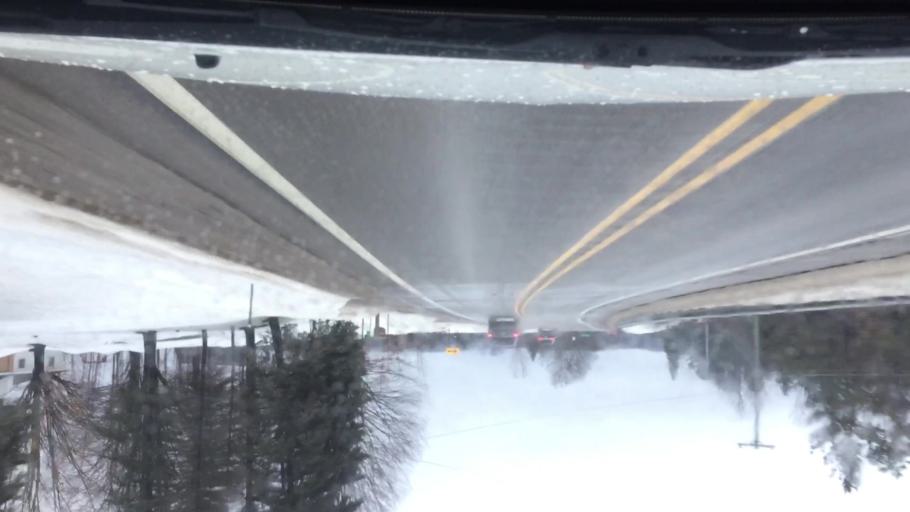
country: US
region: Michigan
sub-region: Charlevoix County
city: East Jordan
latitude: 45.1867
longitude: -85.1653
